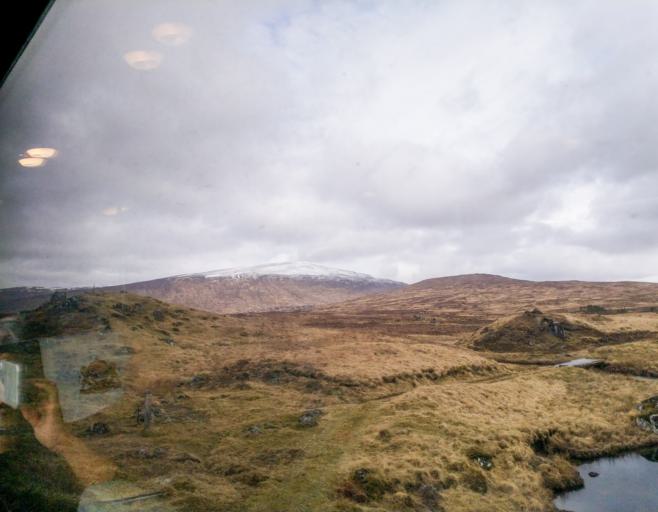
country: GB
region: Scotland
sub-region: Highland
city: Spean Bridge
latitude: 56.7410
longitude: -4.6657
